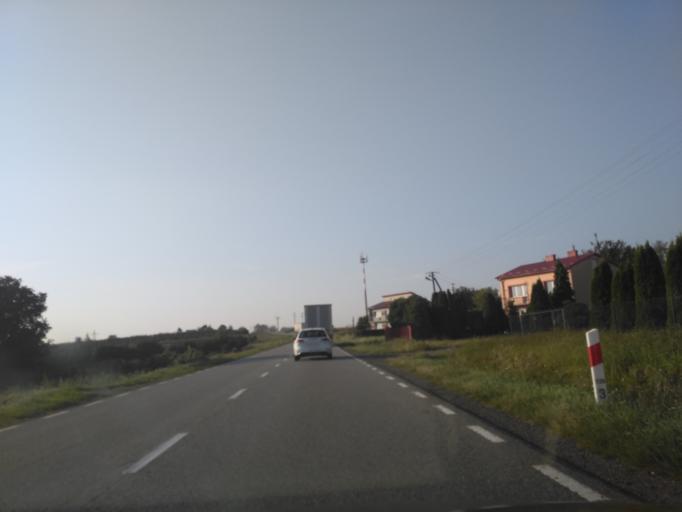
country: PL
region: Lublin Voivodeship
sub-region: Powiat krasnicki
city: Szastarka
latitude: 50.8213
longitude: 22.3154
